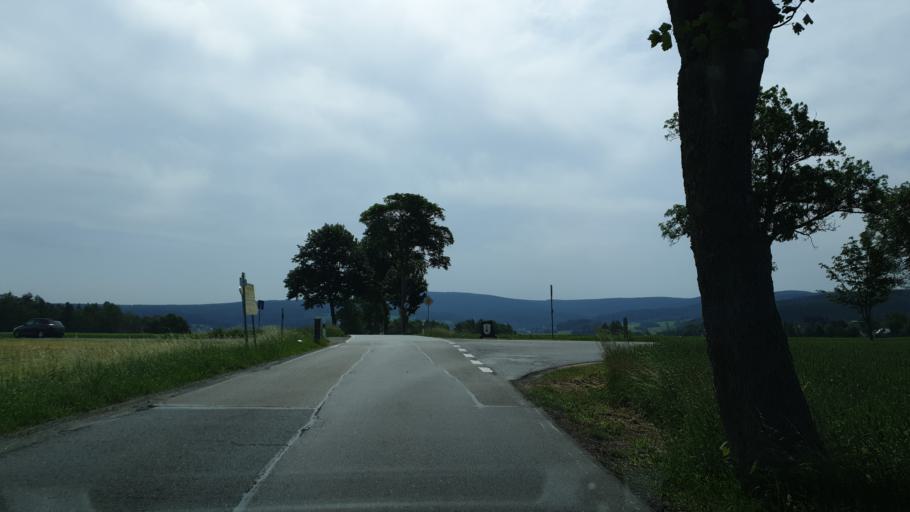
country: DE
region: Saxony
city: Zschorlau
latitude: 50.5563
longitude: 12.6495
